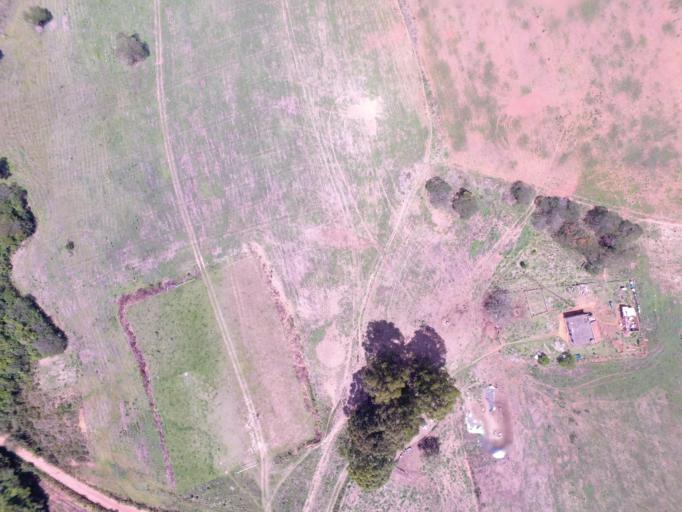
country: BR
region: Minas Gerais
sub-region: Barroso
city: Barroso
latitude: -21.0410
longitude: -44.0030
